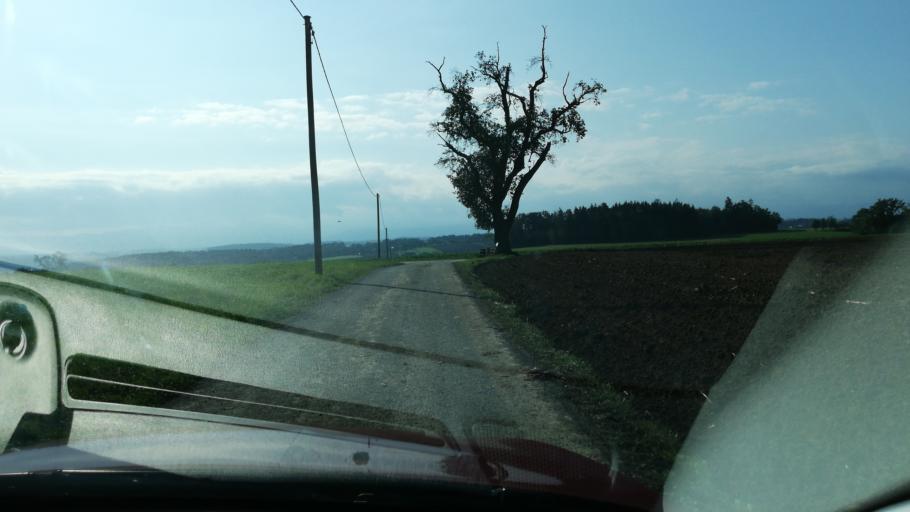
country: AT
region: Upper Austria
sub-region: Politischer Bezirk Kirchdorf an der Krems
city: Kremsmunster
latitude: 48.0952
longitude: 14.1669
